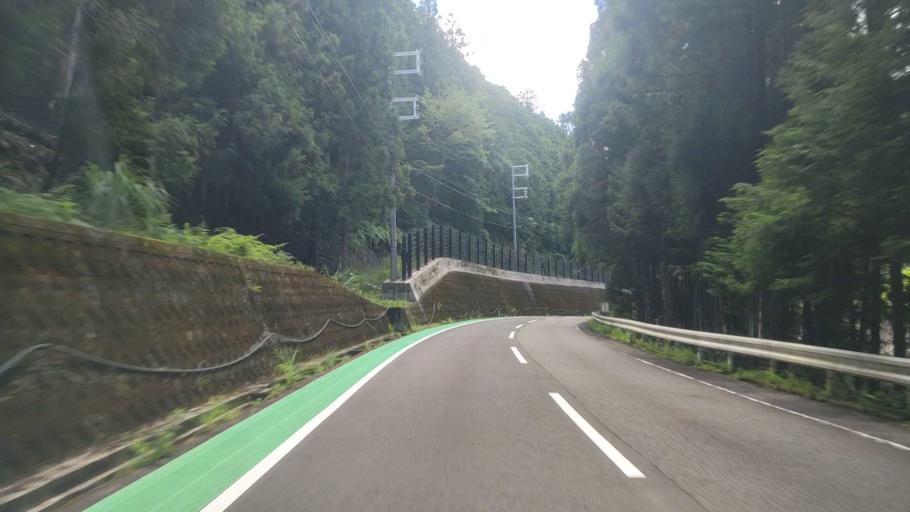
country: JP
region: Mie
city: Owase
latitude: 33.9642
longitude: 135.9931
